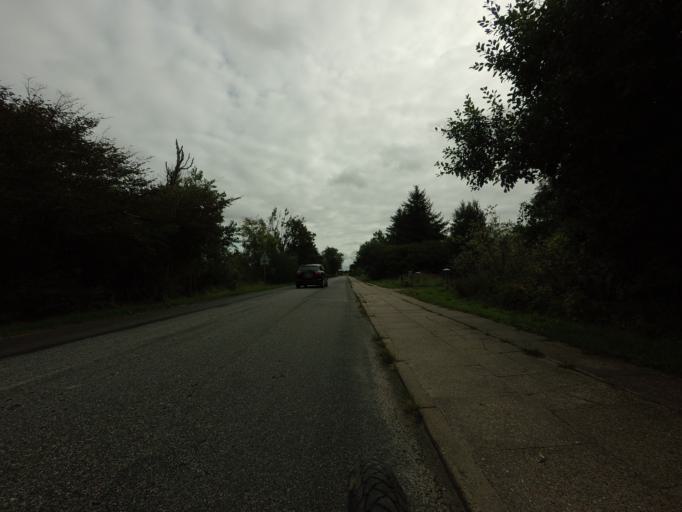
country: DK
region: North Denmark
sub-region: Hjorring Kommune
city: Hirtshals
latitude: 57.5557
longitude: 9.9286
